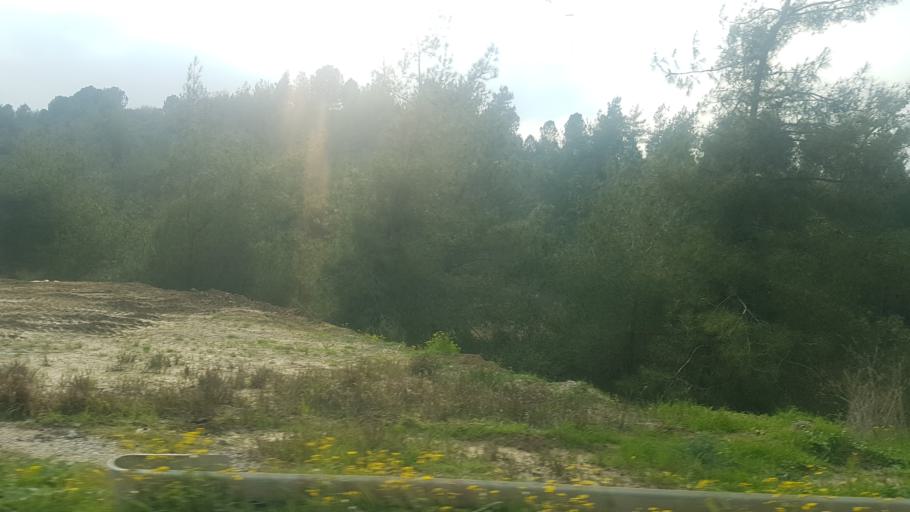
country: TR
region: Mersin
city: Yenice
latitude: 37.0842
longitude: 35.1735
